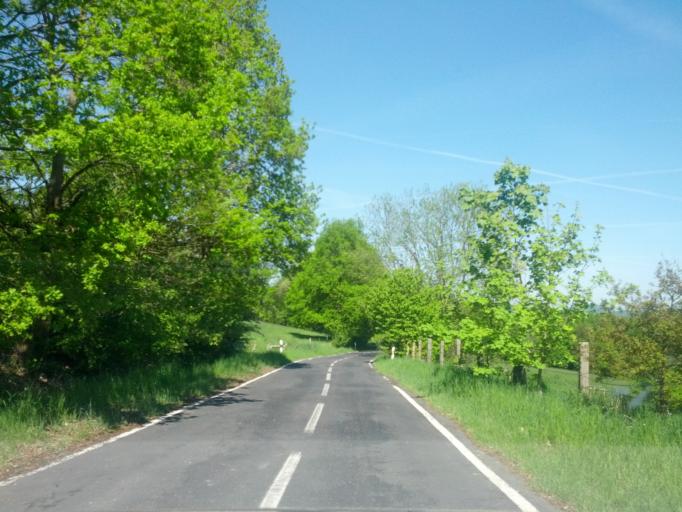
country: DE
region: Thuringia
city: Treffurt
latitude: 51.1233
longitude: 10.1784
